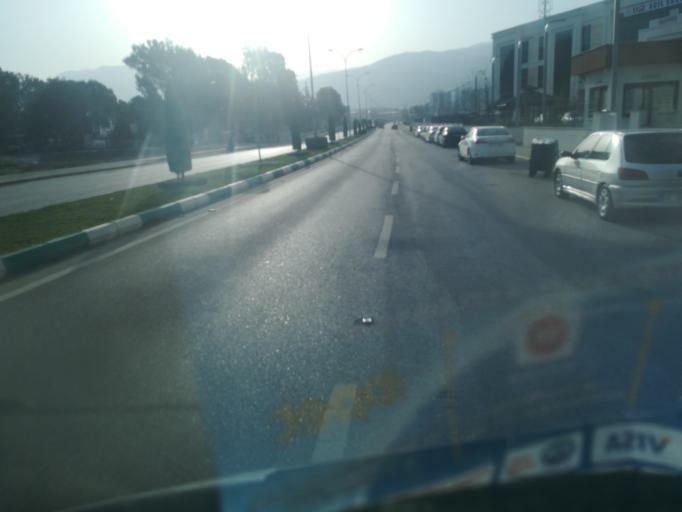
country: TR
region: Osmaniye
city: Osmaniye
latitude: 37.0584
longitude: 36.2172
